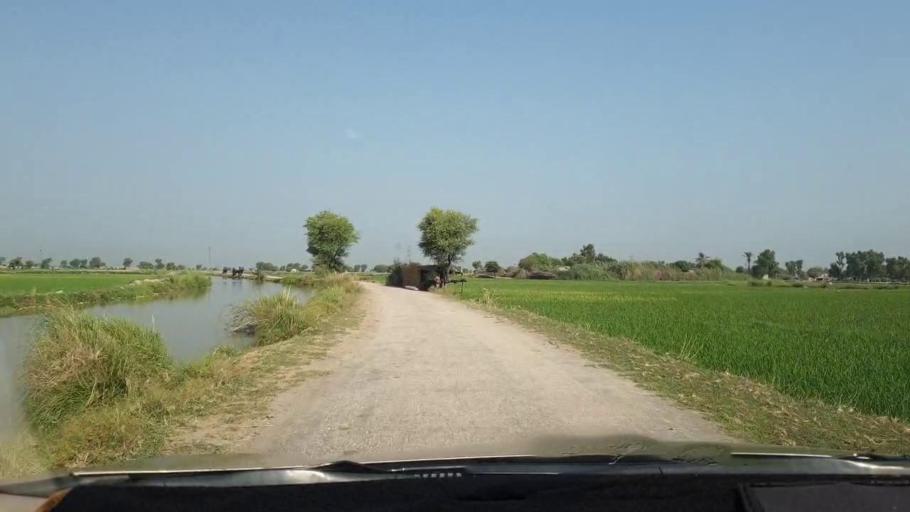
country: PK
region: Sindh
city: Larkana
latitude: 27.6393
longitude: 68.2350
